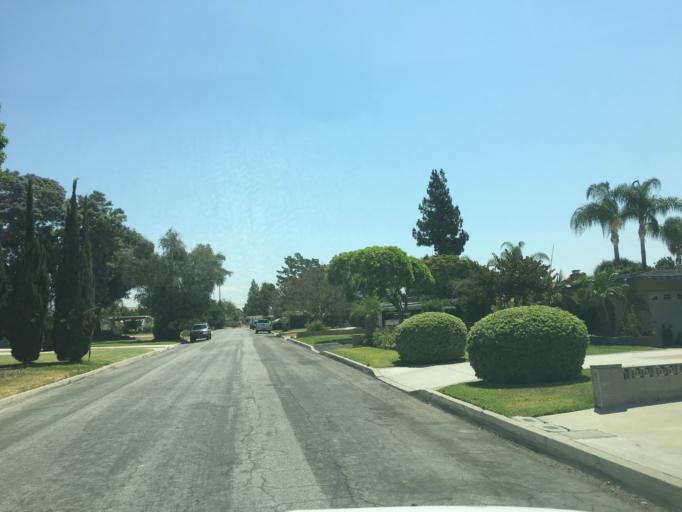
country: US
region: California
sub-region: Los Angeles County
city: Citrus
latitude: 34.1268
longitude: -117.8810
